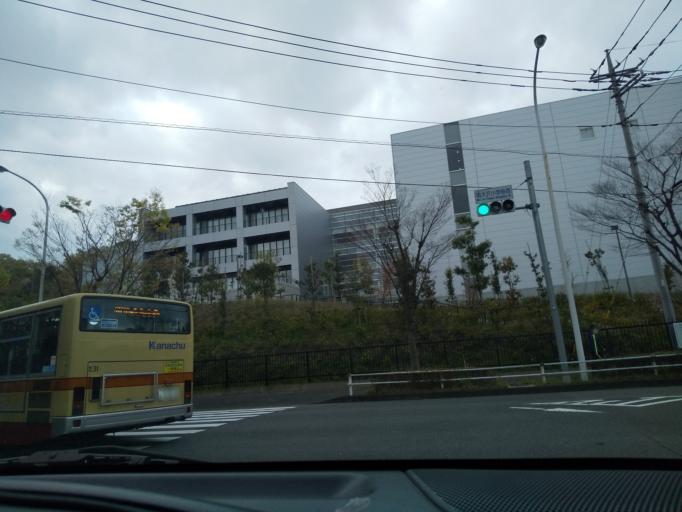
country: JP
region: Tokyo
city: Hachioji
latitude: 35.6081
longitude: 139.3735
